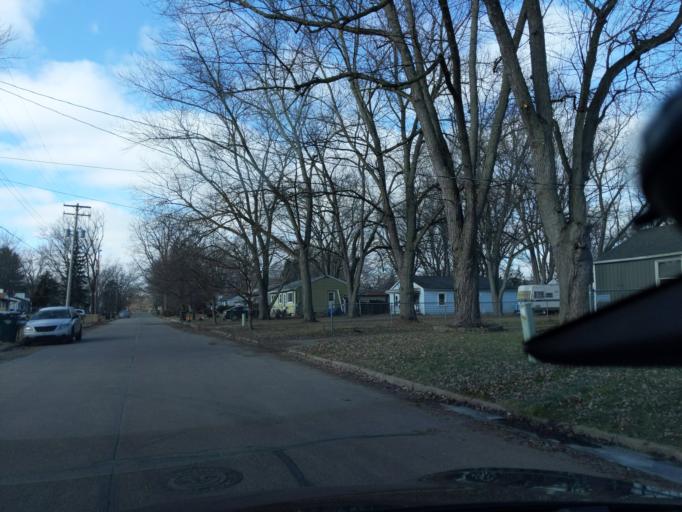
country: US
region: Michigan
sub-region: Ingham County
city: Lansing
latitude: 42.6820
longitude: -84.5880
